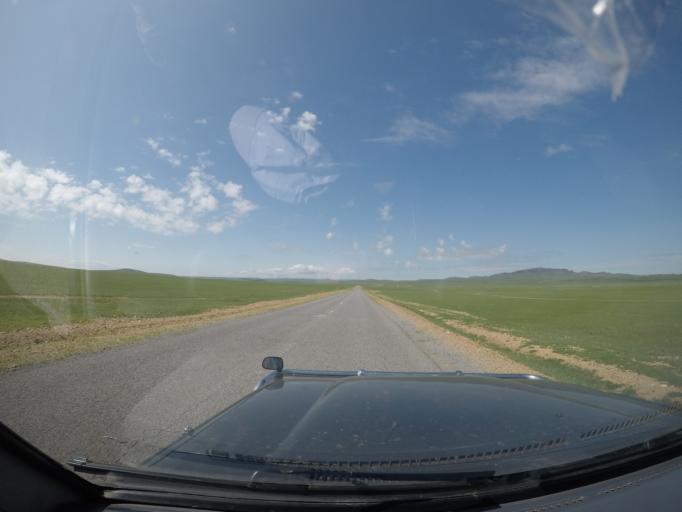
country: MN
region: Hentiy
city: Dundburd
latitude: 47.3439
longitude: 111.4888
